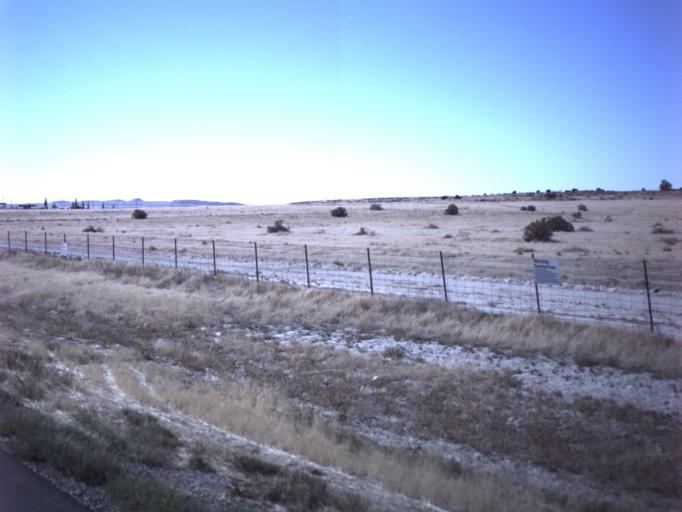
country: US
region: Utah
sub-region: Tooele County
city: Grantsville
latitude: 40.2375
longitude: -112.7233
